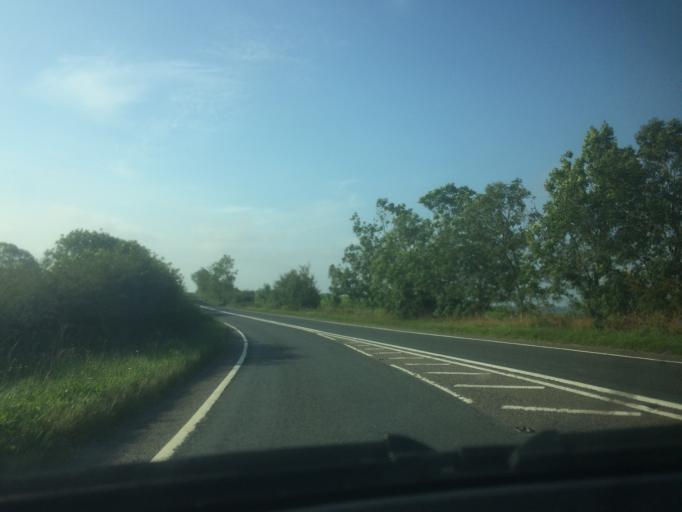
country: GB
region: England
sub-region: Cornwall
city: Pillaton
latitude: 50.4508
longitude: -4.2559
